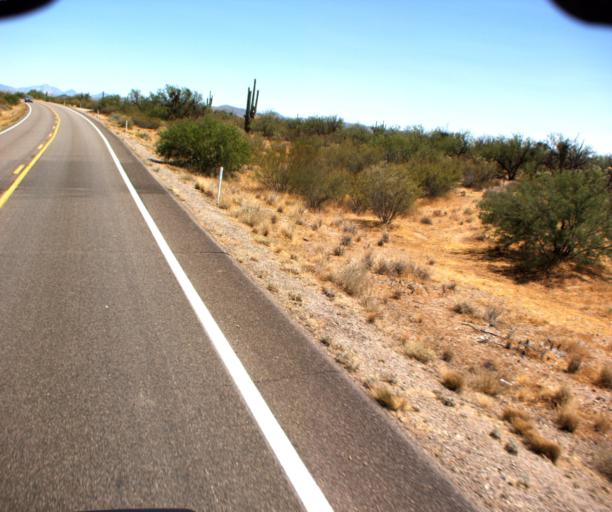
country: US
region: Arizona
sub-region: Pima County
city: Catalina
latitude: 32.6969
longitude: -111.0884
